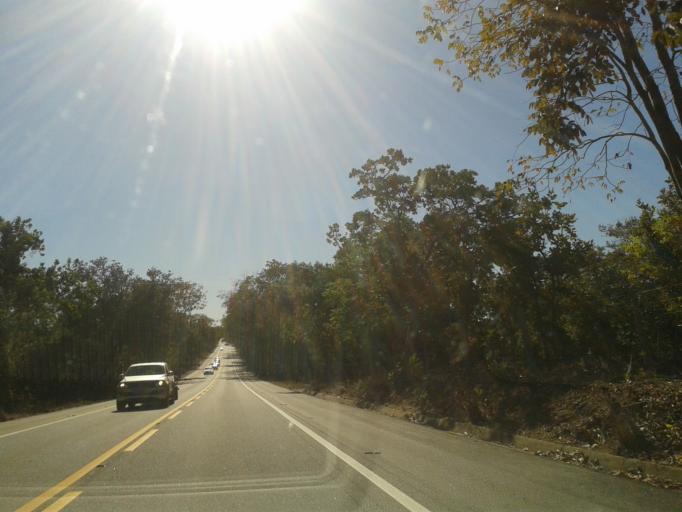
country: BR
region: Goias
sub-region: Itapuranga
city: Itapuranga
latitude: -15.4761
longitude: -50.3386
